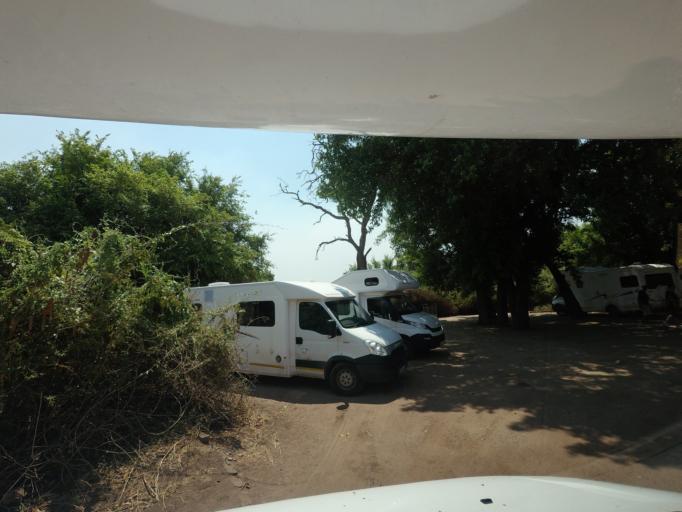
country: BW
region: North West
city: Kasane
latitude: -17.8089
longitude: 25.1452
